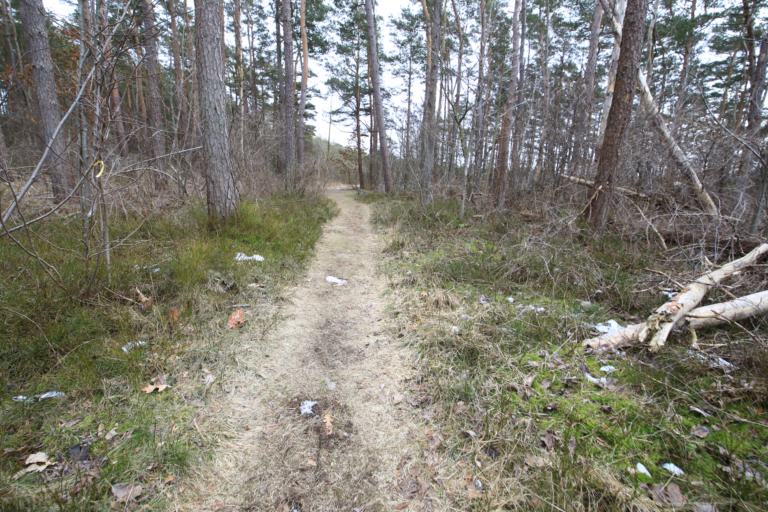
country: SE
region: Halland
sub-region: Kungsbacka Kommun
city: Frillesas
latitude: 57.2365
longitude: 12.1061
